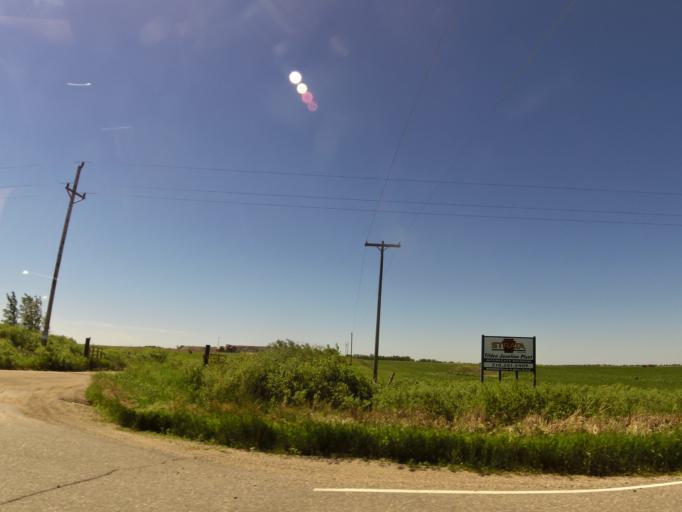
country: US
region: Minnesota
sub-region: Red Lake County
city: Red Lake Falls
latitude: 47.7603
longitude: -96.3424
